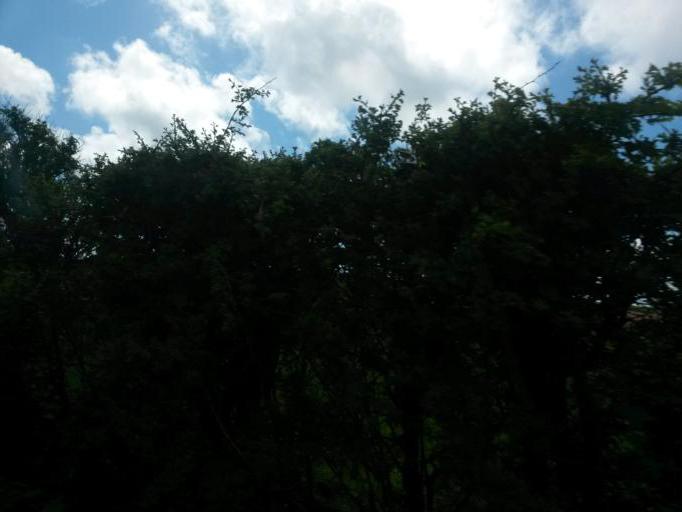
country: IE
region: Munster
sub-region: Waterford
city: Dunmore East
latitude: 52.1932
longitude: -6.8995
